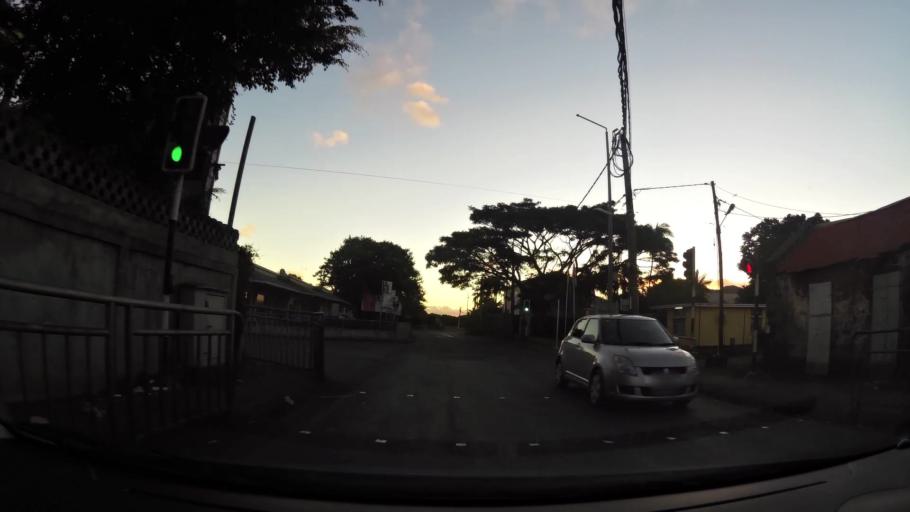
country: MU
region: Moka
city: Saint Pierre
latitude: -20.2242
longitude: 57.5260
